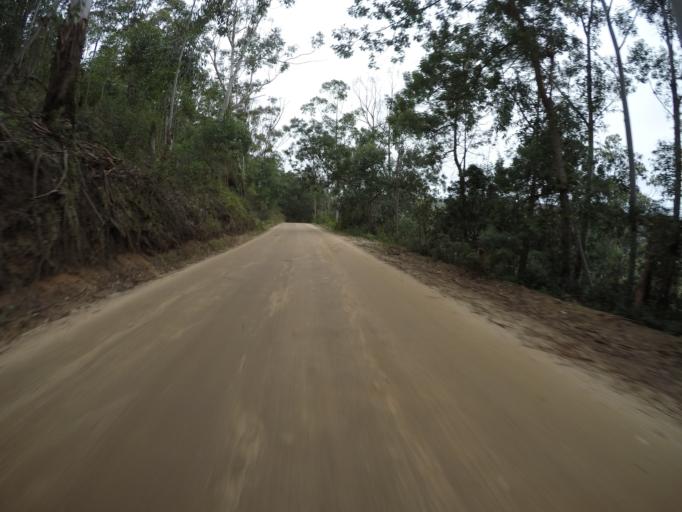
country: ZA
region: Western Cape
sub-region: Eden District Municipality
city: Knysna
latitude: -34.0126
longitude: 22.8087
